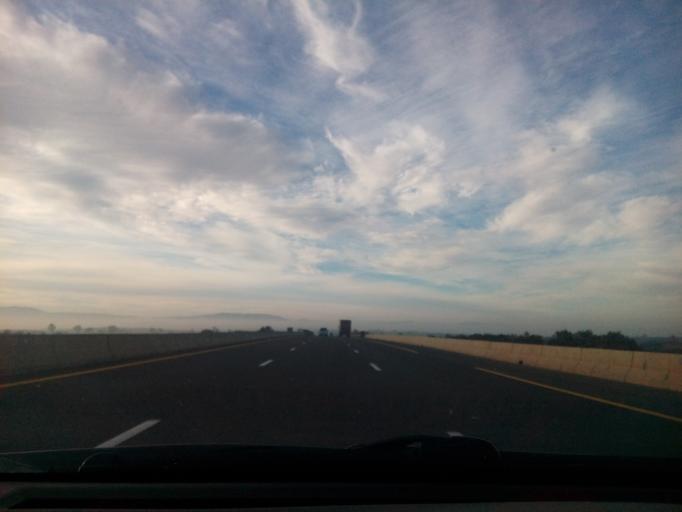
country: DZ
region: Relizane
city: Relizane
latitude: 35.7243
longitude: 0.3012
